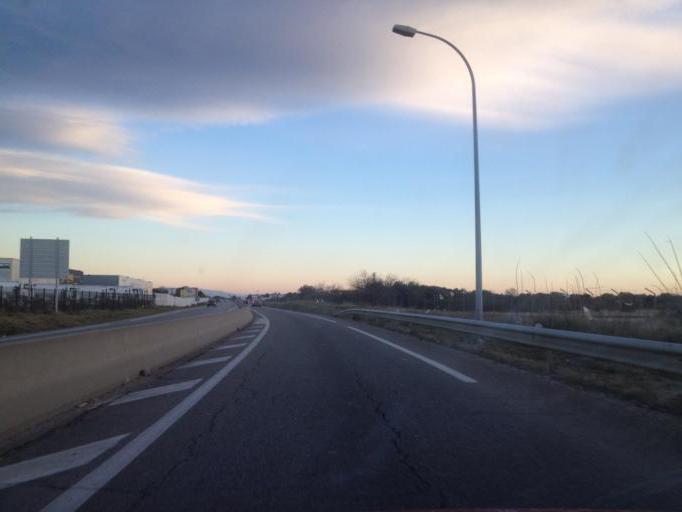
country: FR
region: Provence-Alpes-Cote d'Azur
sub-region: Departement du Vaucluse
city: Orange
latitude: 44.1172
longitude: 4.8382
